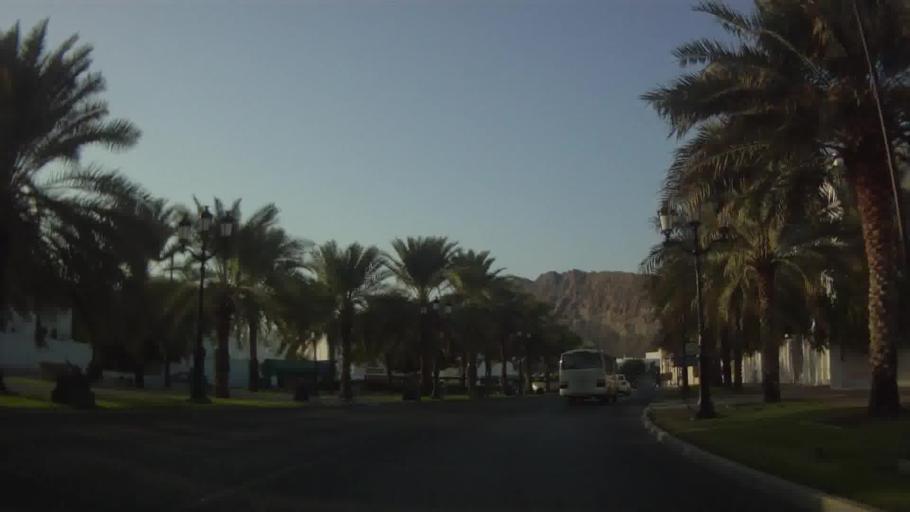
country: OM
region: Muhafazat Masqat
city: Muscat
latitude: 23.6132
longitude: 58.5915
